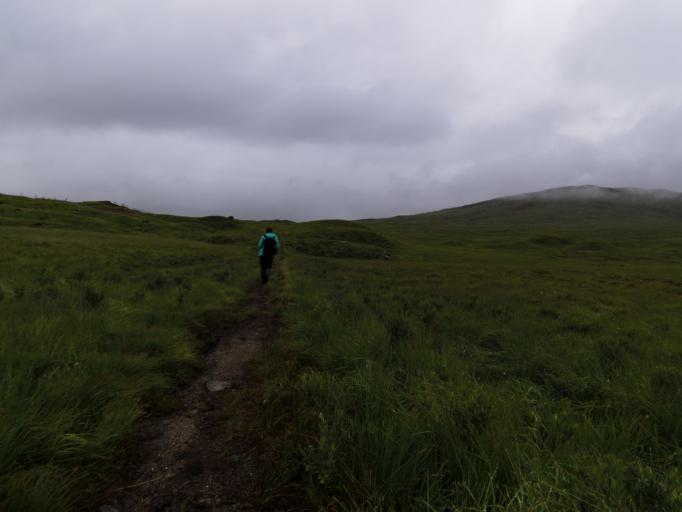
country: GB
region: Scotland
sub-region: Highland
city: Spean Bridge
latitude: 56.7722
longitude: -4.7107
